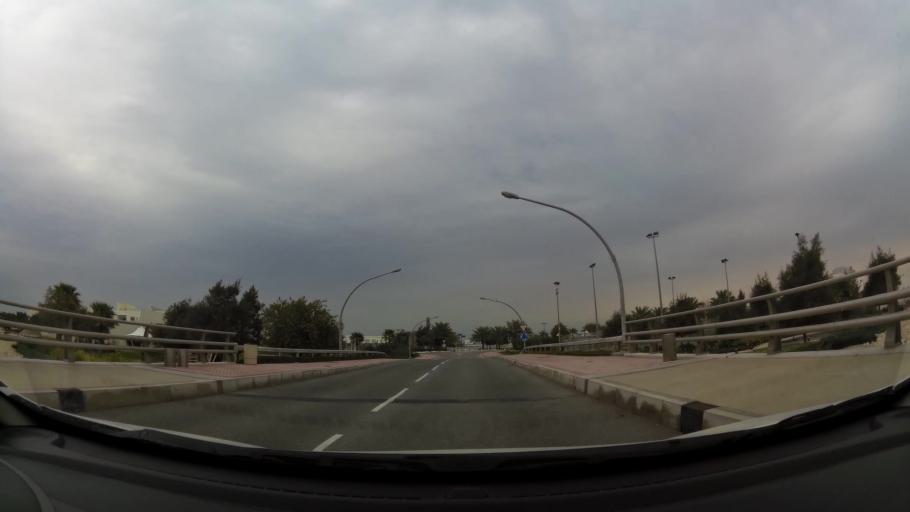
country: BH
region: Central Governorate
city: Dar Kulayb
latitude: 25.8452
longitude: 50.6172
